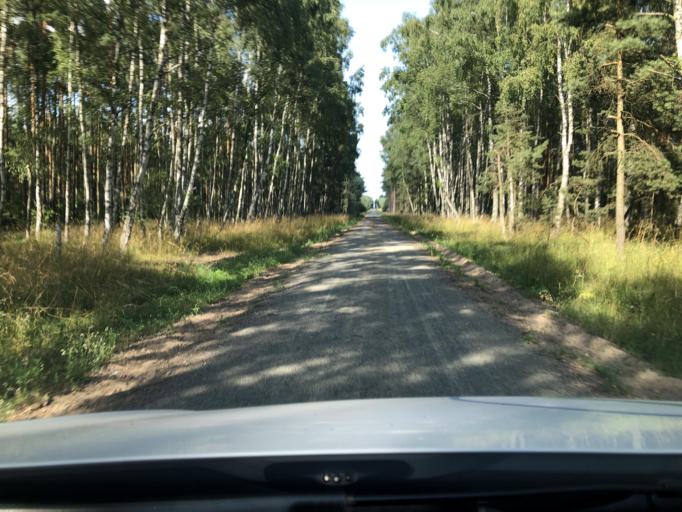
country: SE
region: Skane
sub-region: Kristianstads Kommun
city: Norra Asum
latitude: 55.9171
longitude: 14.1192
